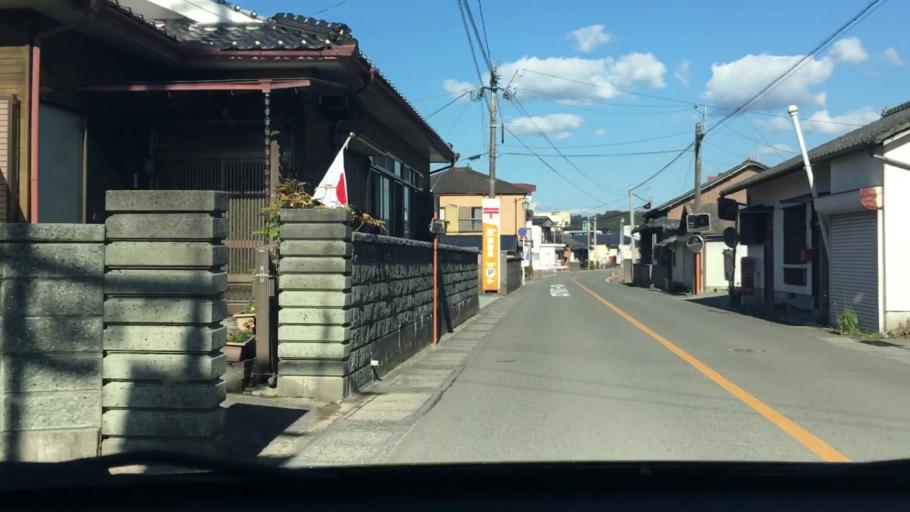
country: JP
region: Kagoshima
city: Satsumasendai
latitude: 31.7870
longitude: 130.4036
